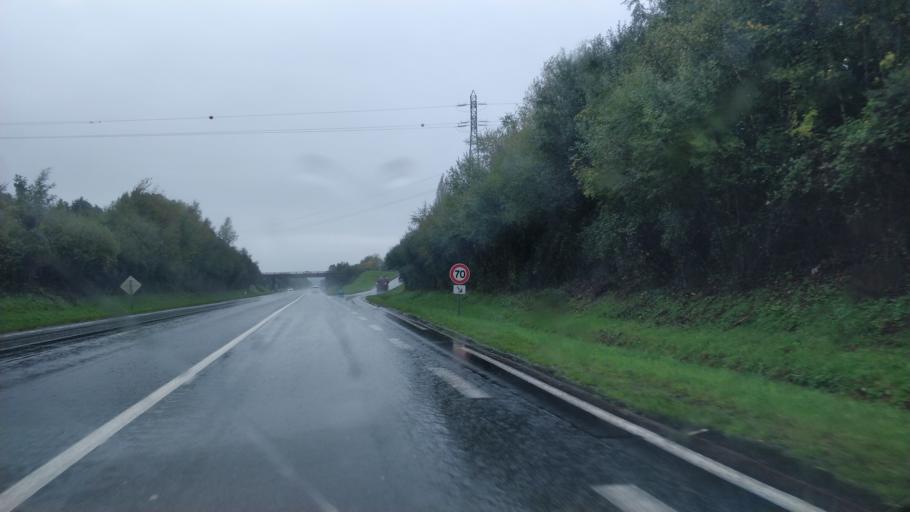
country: FR
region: Lower Normandy
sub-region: Departement de la Manche
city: Saint-Planchers
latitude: 48.8399
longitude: -1.5395
